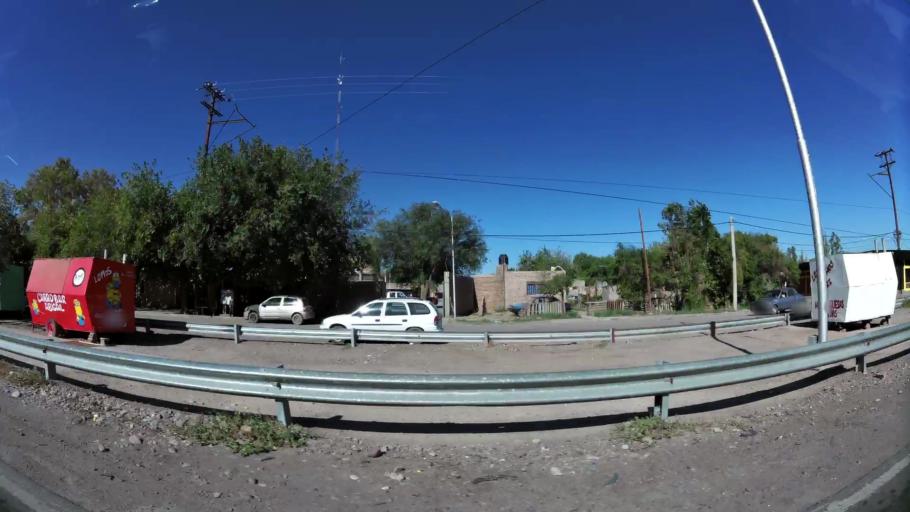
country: AR
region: San Juan
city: Villa Paula de Sarmiento
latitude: -31.5124
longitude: -68.5176
